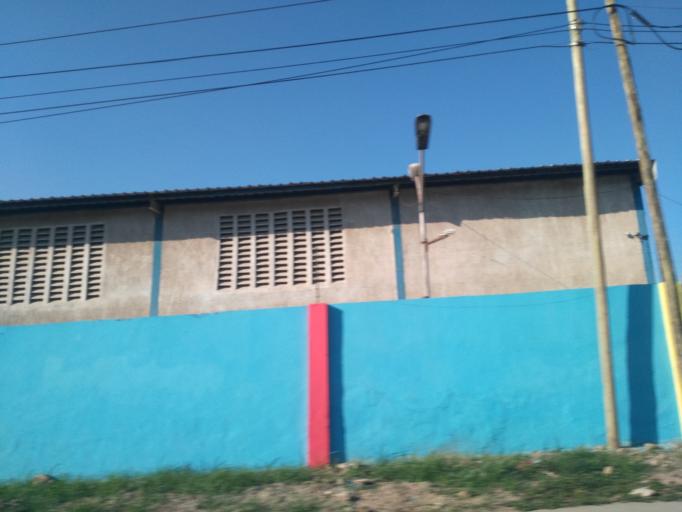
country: TZ
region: Dar es Salaam
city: Magomeni
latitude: -6.7614
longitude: 39.2404
